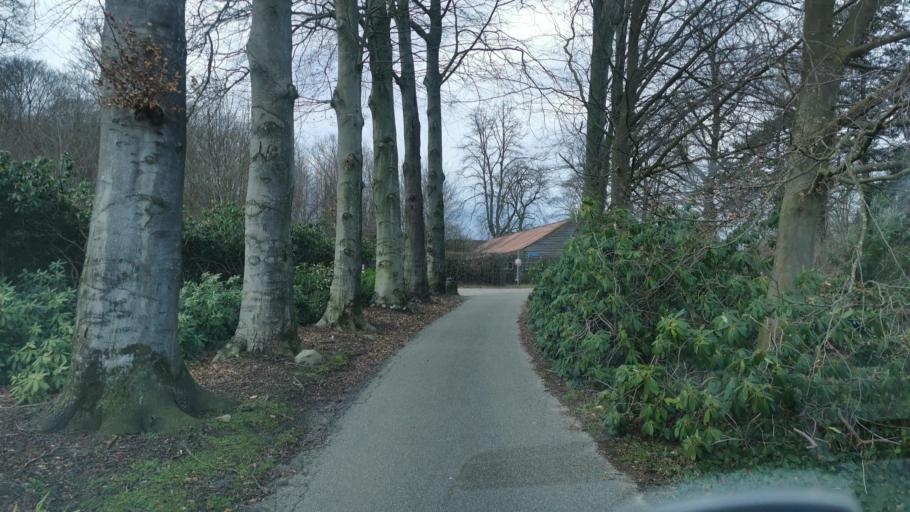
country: NL
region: Overijssel
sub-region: Gemeente Oldenzaal
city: Oldenzaal
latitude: 52.3083
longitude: 6.9606
